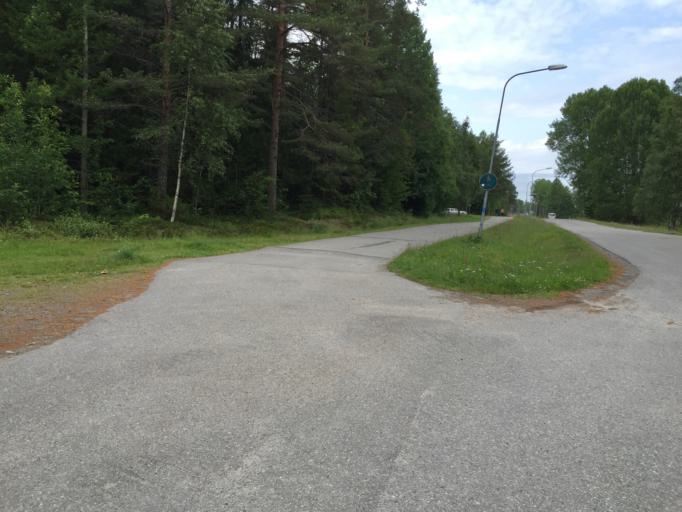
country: SE
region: Vaesterbotten
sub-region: Umea Kommun
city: Ersmark
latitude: 63.8389
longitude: 20.3389
